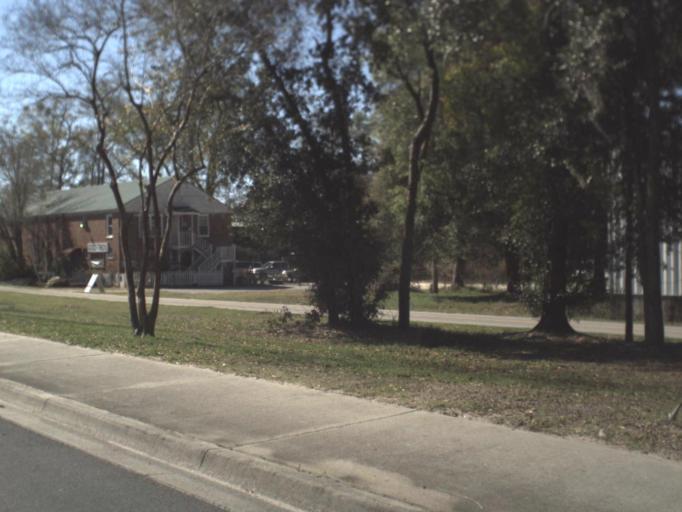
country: US
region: Florida
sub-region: Leon County
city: Tallahassee
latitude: 30.4026
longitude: -84.2823
